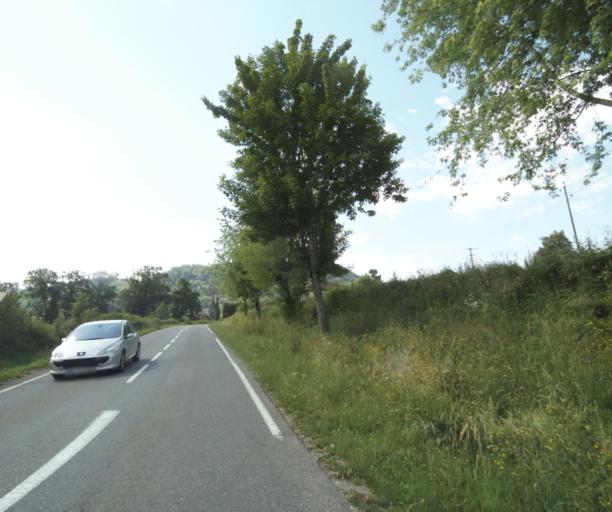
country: FR
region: Rhone-Alpes
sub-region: Departement de la Haute-Savoie
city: Allinges
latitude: 46.3403
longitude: 6.4623
